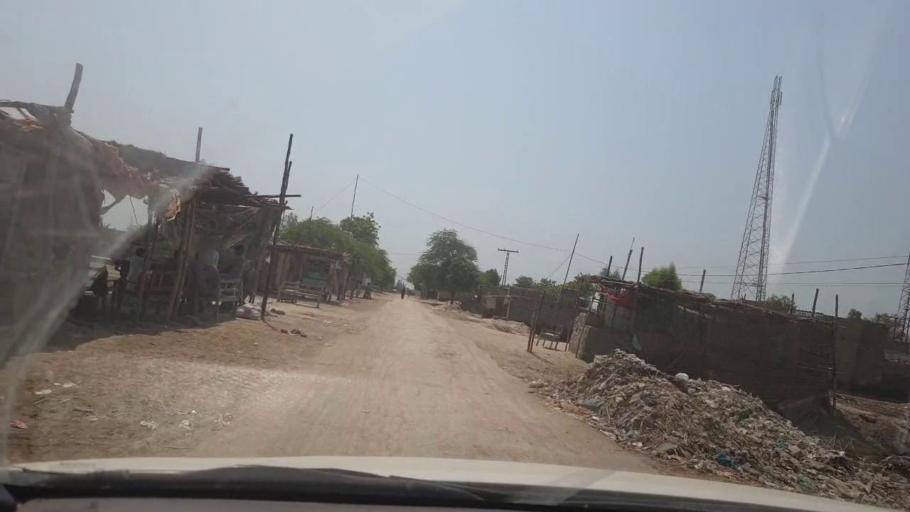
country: PK
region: Sindh
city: Lakhi
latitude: 27.8595
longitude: 68.7109
